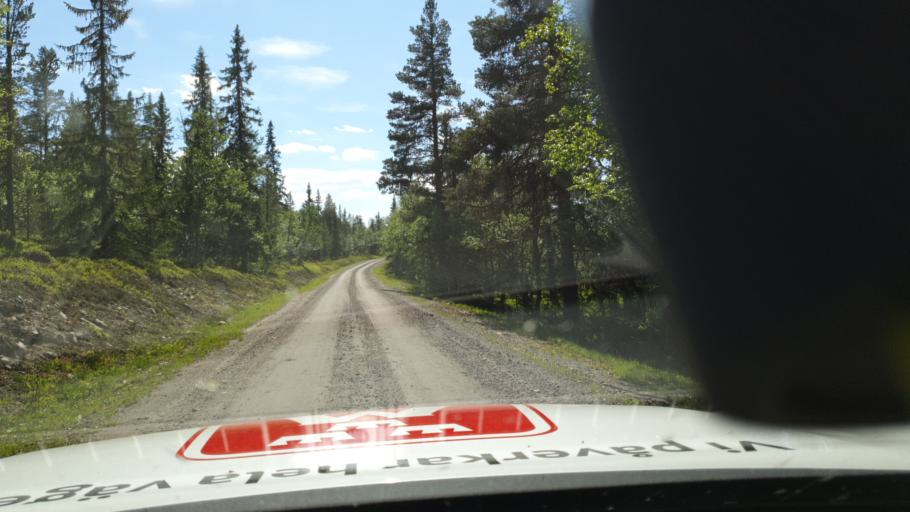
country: NO
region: Hedmark
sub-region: Engerdal
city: Engerdal
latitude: 62.1432
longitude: 12.9481
